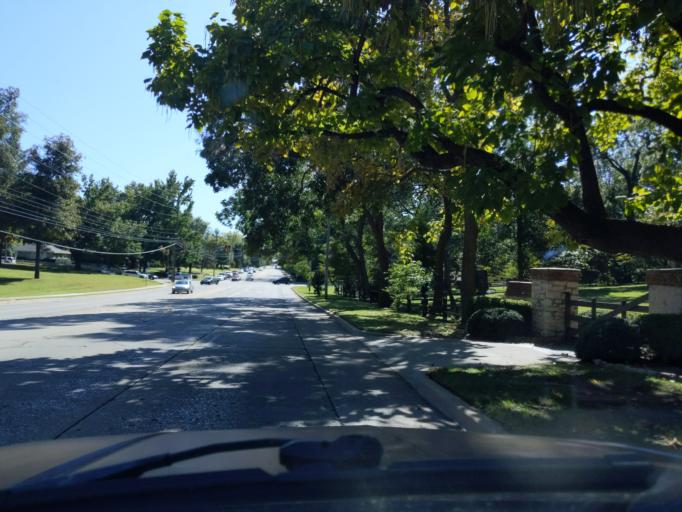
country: US
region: Oklahoma
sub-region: Tulsa County
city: Tulsa
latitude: 36.1053
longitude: -95.9580
